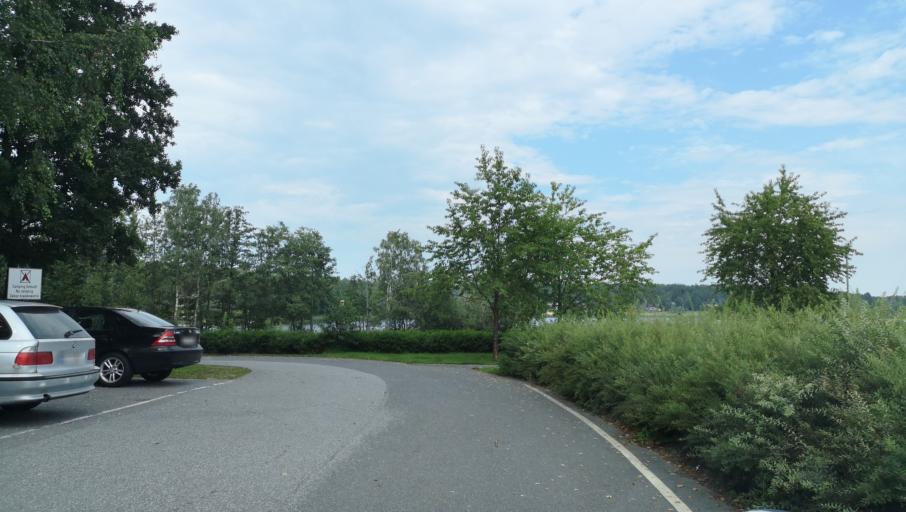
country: NO
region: Ostfold
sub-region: Rygge
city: Rygge
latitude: 59.4615
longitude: 10.7683
